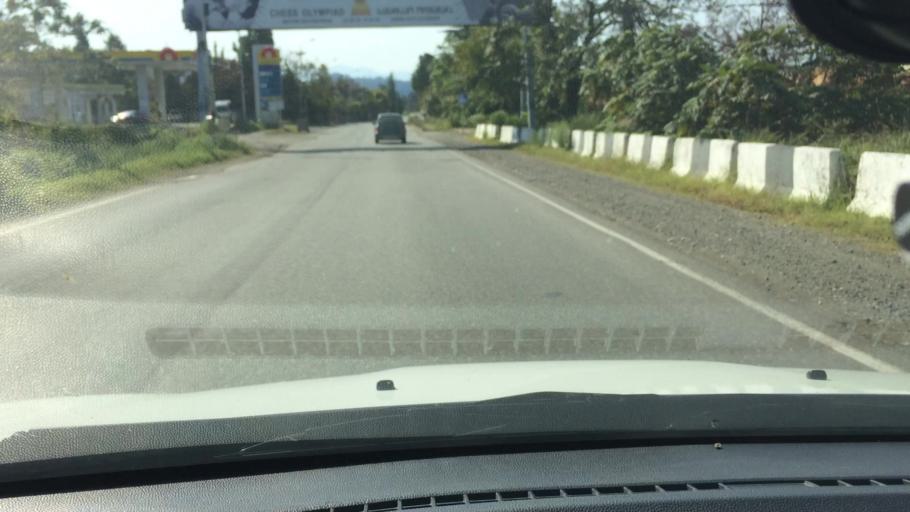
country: GE
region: Ajaria
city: Makhinjauri
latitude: 41.7360
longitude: 41.7341
